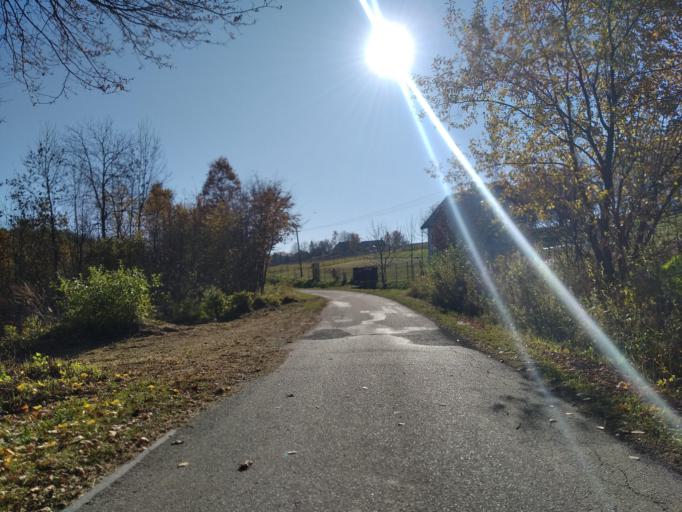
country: PL
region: Subcarpathian Voivodeship
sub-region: Powiat strzyzowski
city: Frysztak
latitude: 49.8501
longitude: 21.5938
